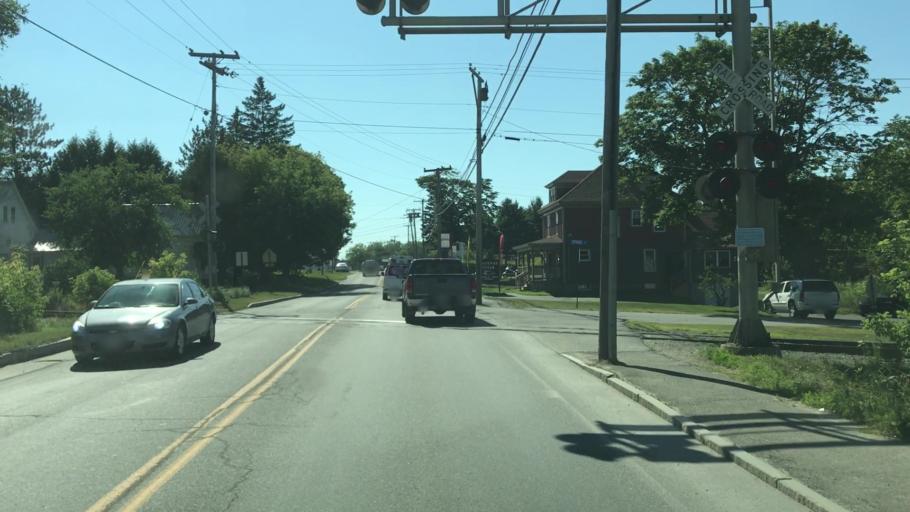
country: US
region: Maine
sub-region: Penobscot County
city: Lincoln
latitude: 45.3631
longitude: -68.5088
